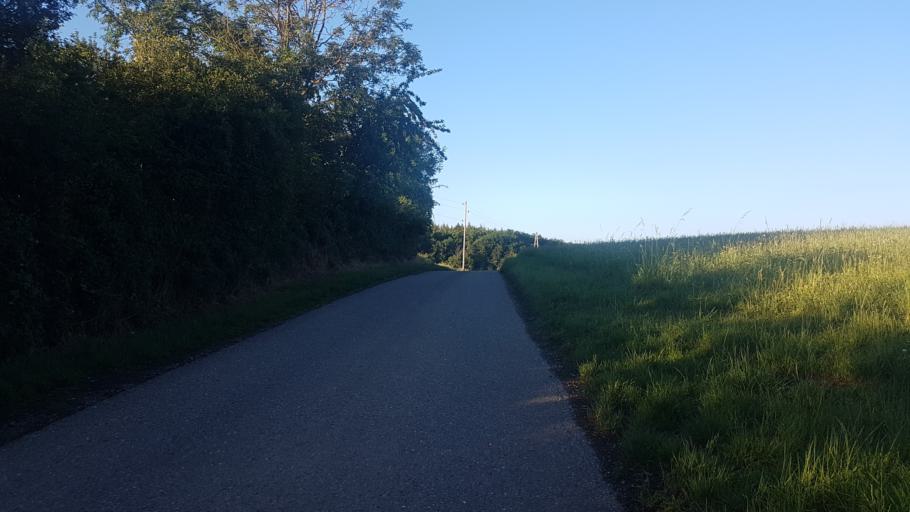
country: DE
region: Baden-Wuerttemberg
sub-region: Regierungsbezirk Stuttgart
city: Pfaffenhofen
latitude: 49.0741
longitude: 8.9558
